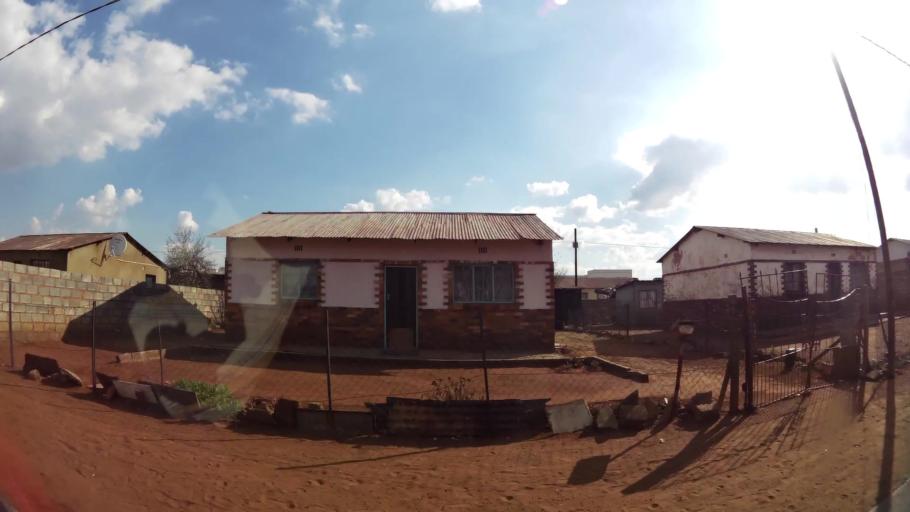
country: ZA
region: Gauteng
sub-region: City of Johannesburg Metropolitan Municipality
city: Soweto
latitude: -26.2212
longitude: 27.8598
